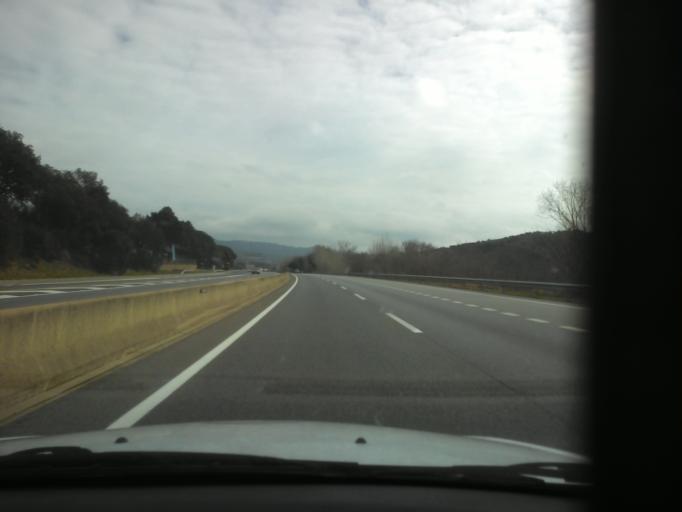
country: ES
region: Catalonia
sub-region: Provincia de Girona
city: Santa Cristina d'Aro
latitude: 41.8268
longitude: 2.9489
